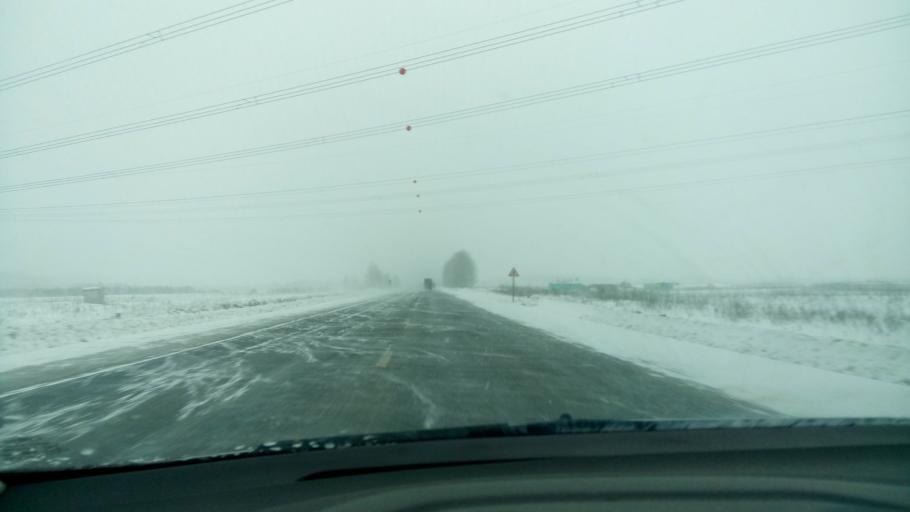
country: RU
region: Sverdlovsk
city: Beloyarskiy
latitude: 56.7743
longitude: 61.5188
